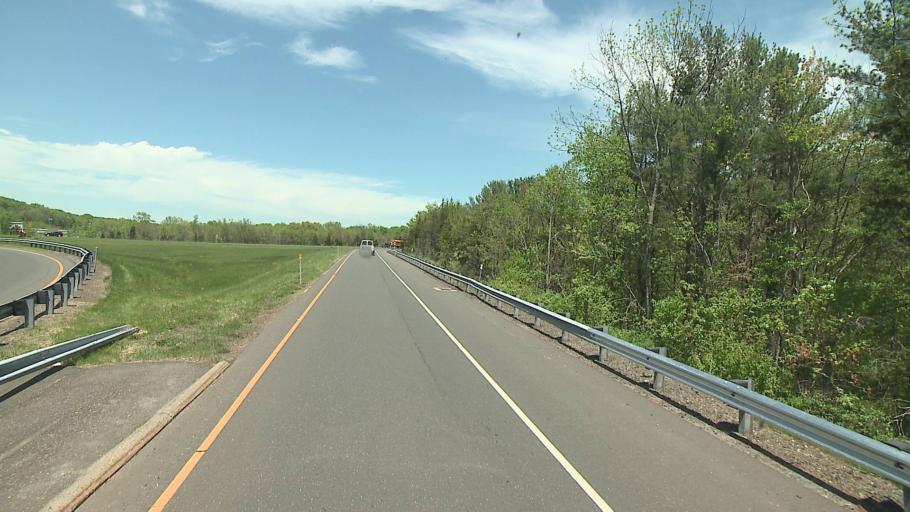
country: US
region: Connecticut
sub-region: New Haven County
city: Middlebury
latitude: 41.4946
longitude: -73.1585
